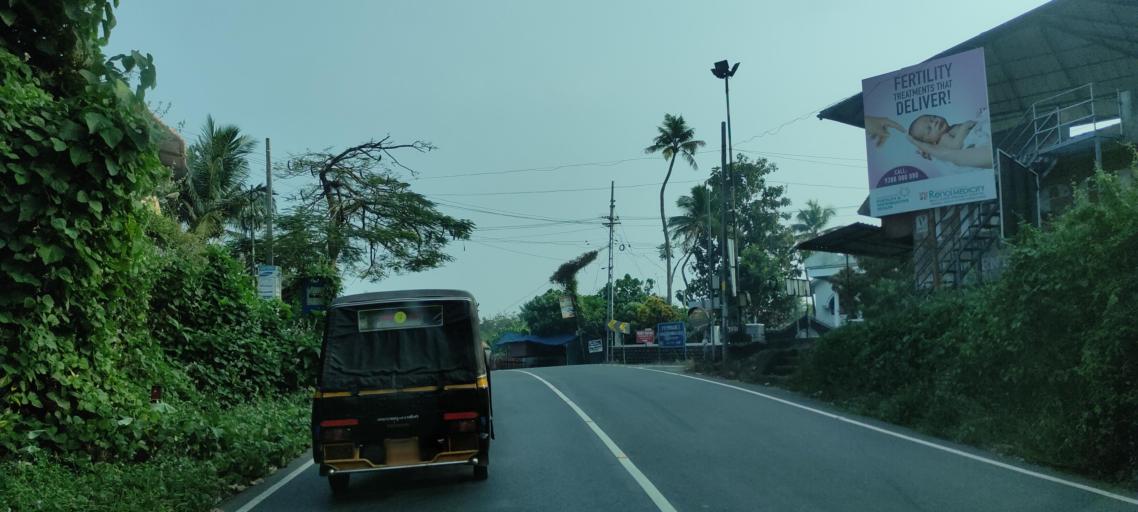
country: IN
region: Kerala
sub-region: Kottayam
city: Vaikam
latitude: 9.7598
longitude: 76.4935
